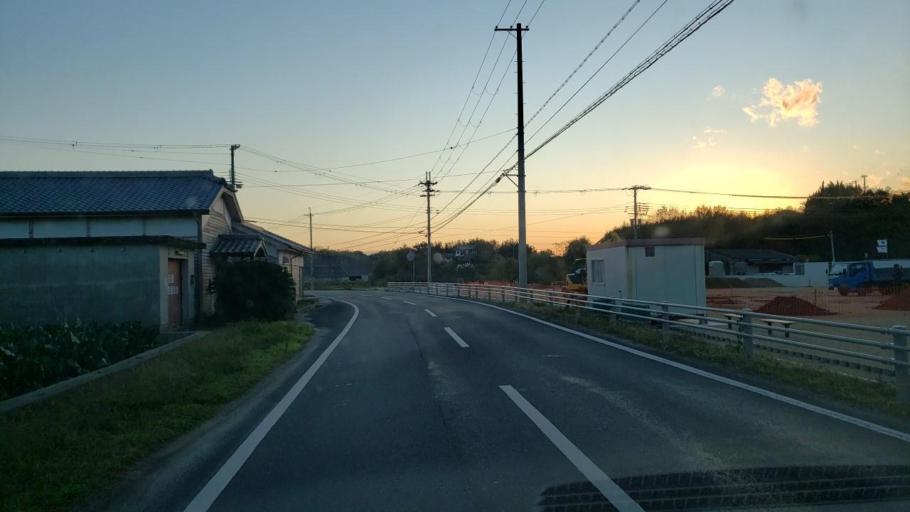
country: JP
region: Hyogo
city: Fukura
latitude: 34.3408
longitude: 134.7806
